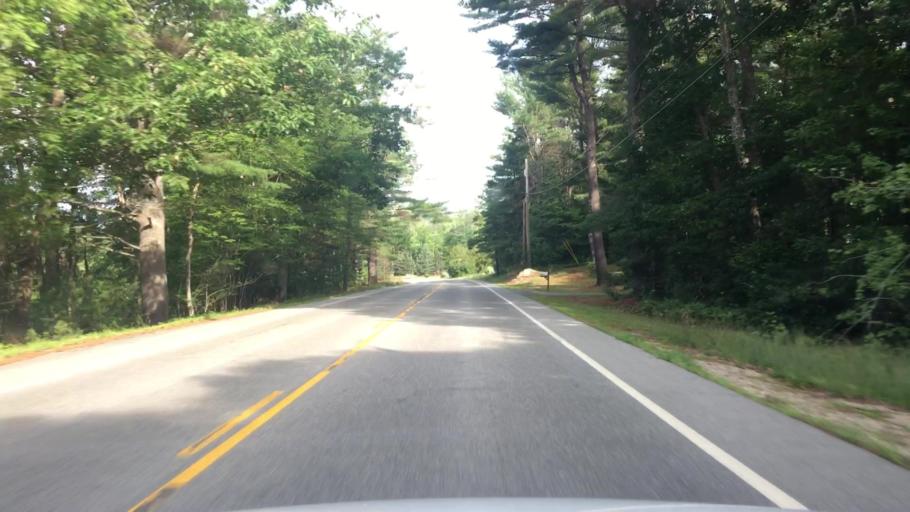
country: US
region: New Hampshire
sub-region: Carroll County
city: Effingham
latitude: 43.7930
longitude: -70.9797
